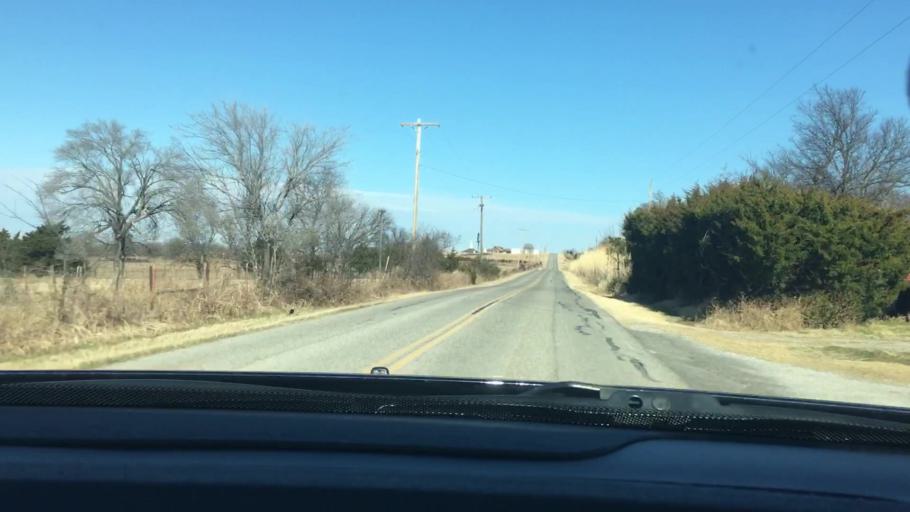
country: US
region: Oklahoma
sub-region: Murray County
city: Davis
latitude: 34.4979
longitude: -97.0553
